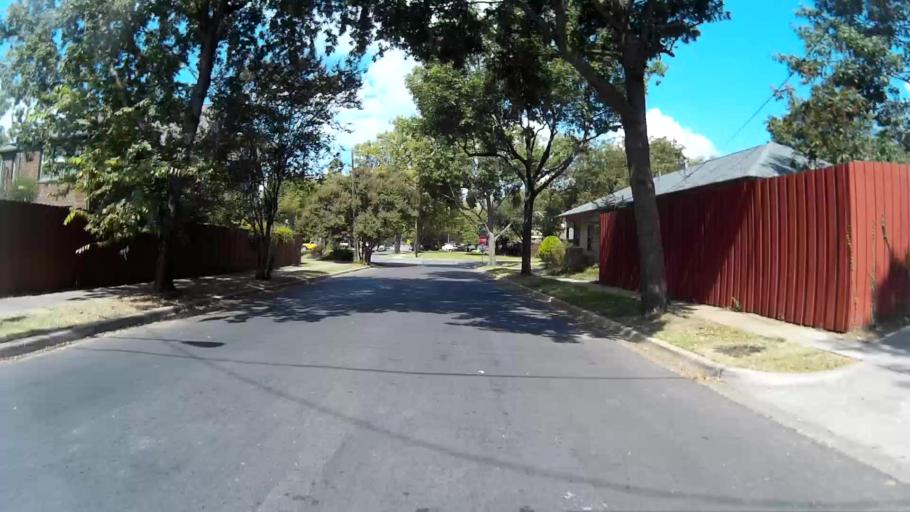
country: US
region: Texas
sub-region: Dallas County
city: Highland Park
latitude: 32.8087
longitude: -96.7551
